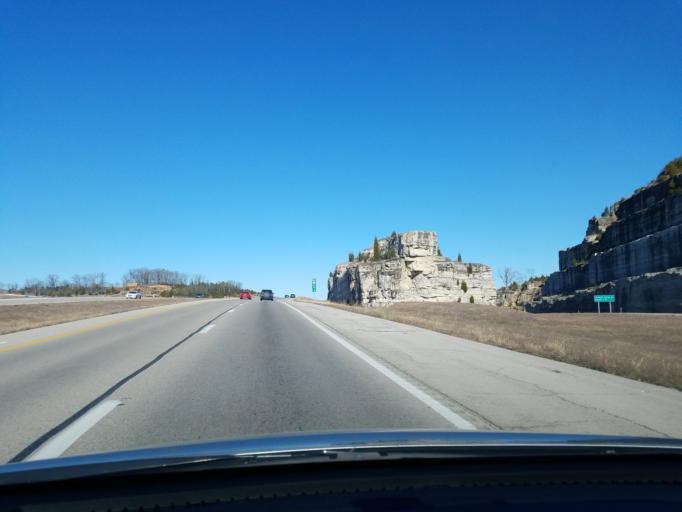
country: US
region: Missouri
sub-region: Taney County
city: Merriam Woods
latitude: 36.7465
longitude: -93.2225
